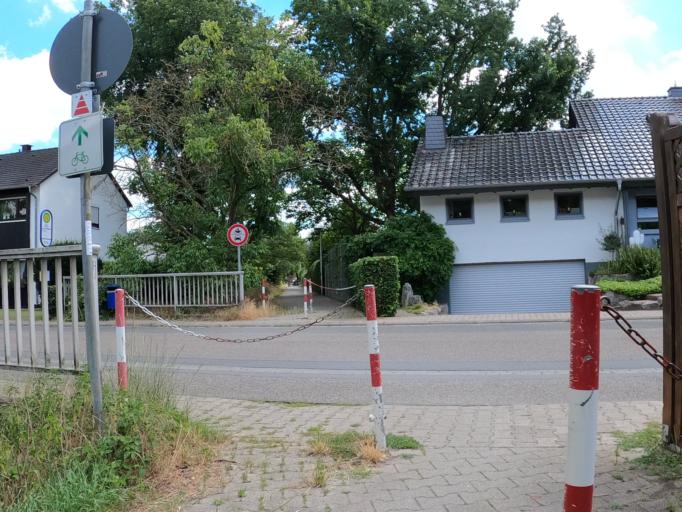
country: DE
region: Hesse
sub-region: Regierungsbezirk Darmstadt
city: Nauheim
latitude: 49.9571
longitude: 8.4640
